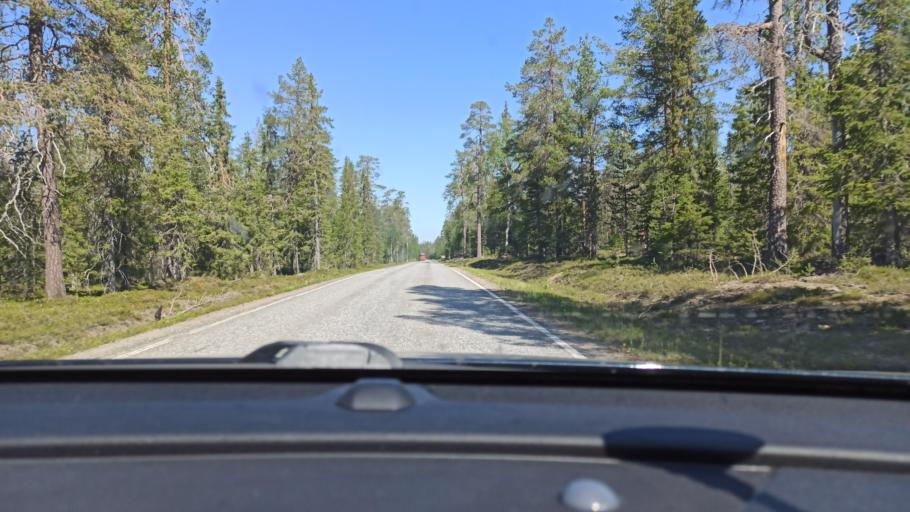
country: FI
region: Lapland
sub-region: Tunturi-Lappi
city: Kolari
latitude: 67.6628
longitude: 24.1643
